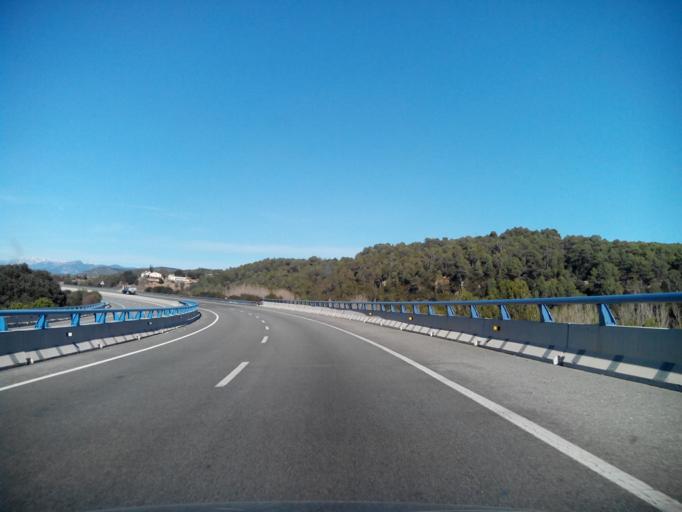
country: ES
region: Catalonia
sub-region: Provincia de Barcelona
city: Navas
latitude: 41.9176
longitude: 1.8844
